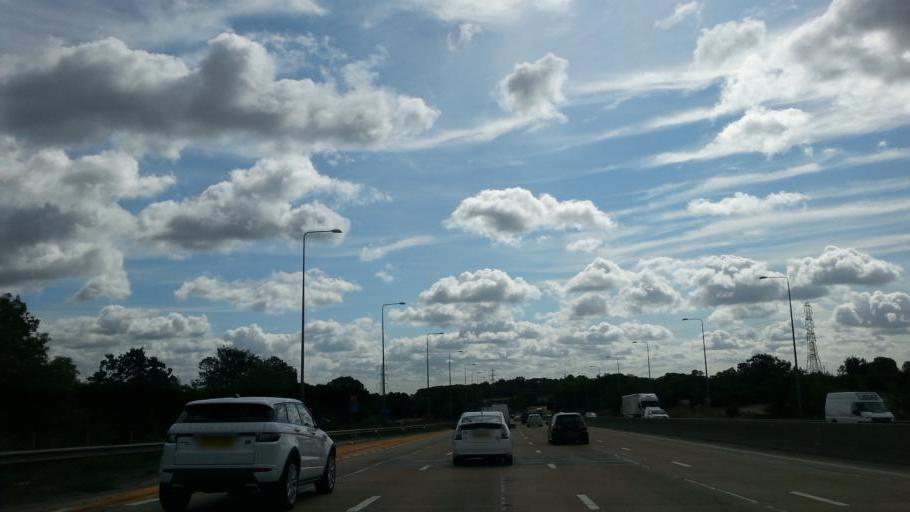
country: GB
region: England
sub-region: Hertfordshire
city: Potters Bar
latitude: 51.6873
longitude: -0.1591
